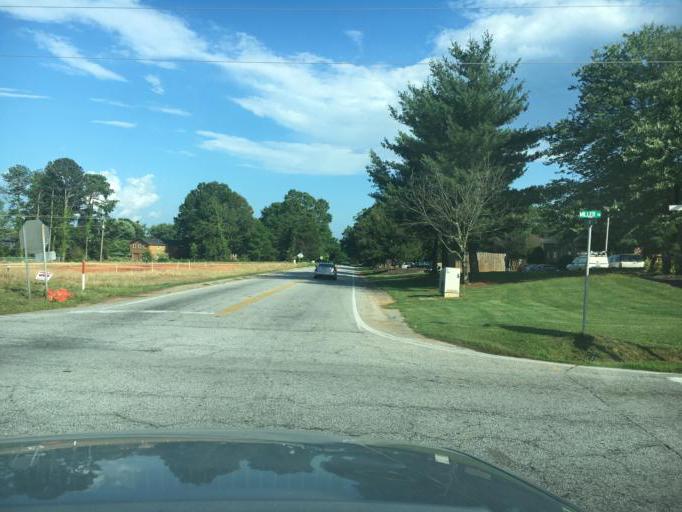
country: US
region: South Carolina
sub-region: Greenville County
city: Mauldin
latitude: 34.7928
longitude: -82.3017
